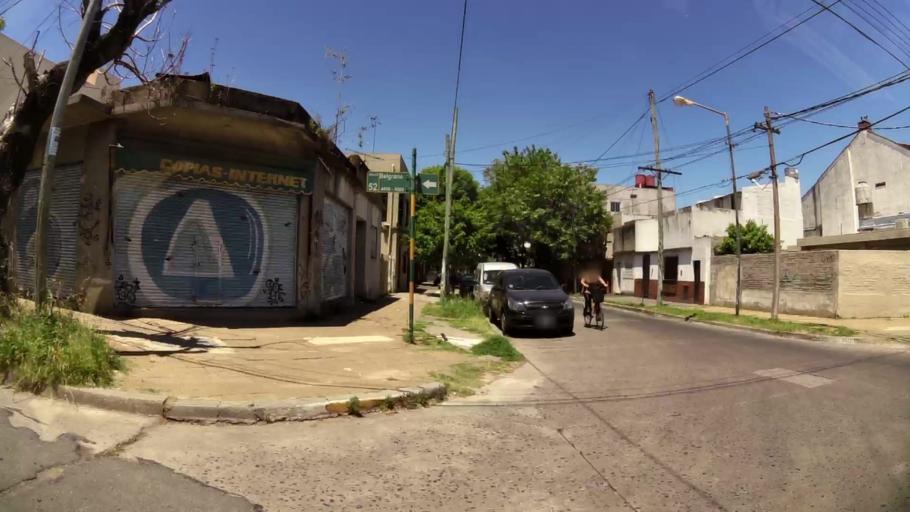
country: AR
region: Buenos Aires
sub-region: Partido de General San Martin
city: General San Martin
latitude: -34.5825
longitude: -58.5430
